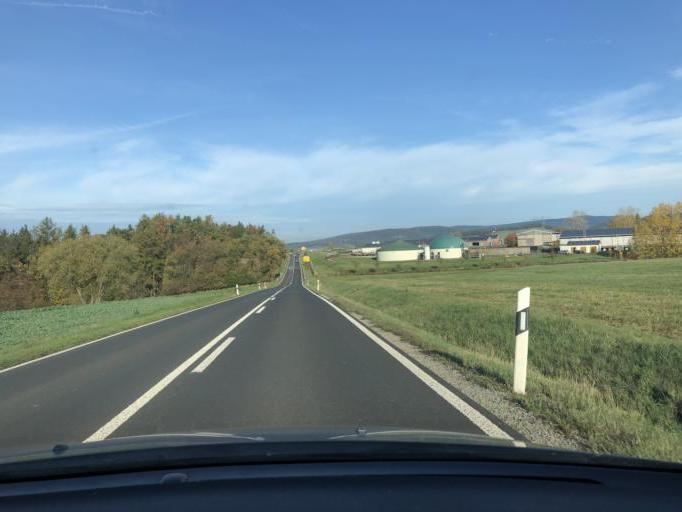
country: DE
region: Thuringia
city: Ehrenberg
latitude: 50.4755
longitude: 10.6539
